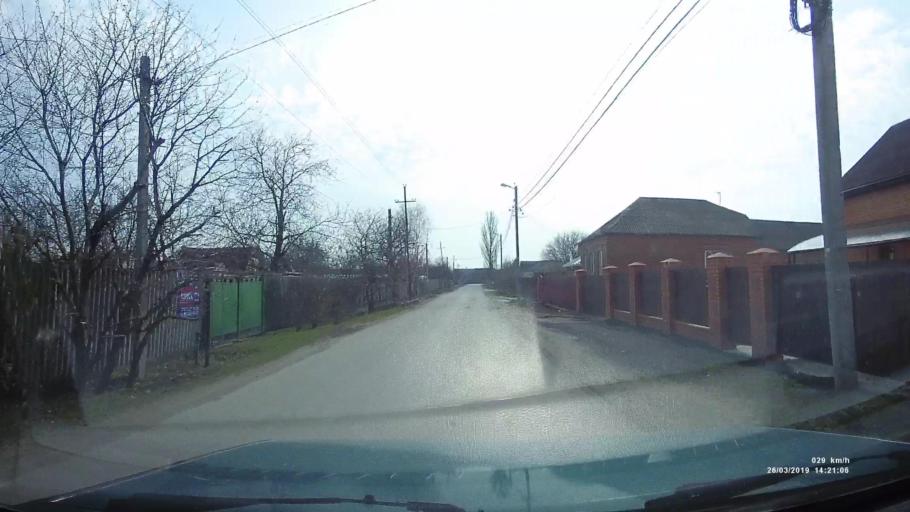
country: RU
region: Rostov
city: Novobessergenovka
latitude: 47.1877
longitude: 38.8695
